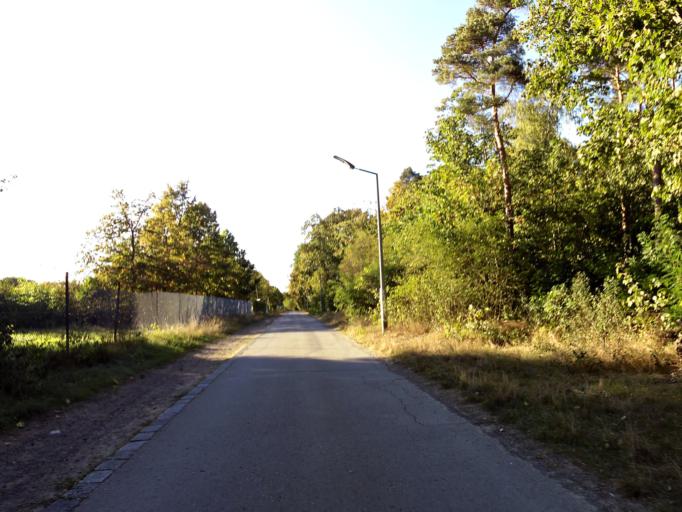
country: DE
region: Berlin
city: Grunewald
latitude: 52.4878
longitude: 13.2539
